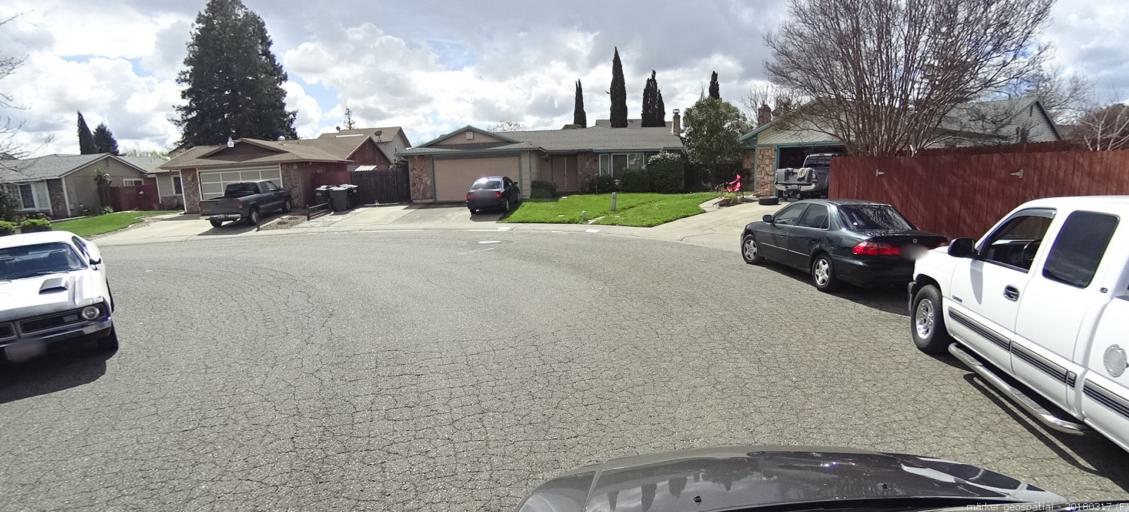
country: US
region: California
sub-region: Sacramento County
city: Florin
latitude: 38.4767
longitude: -121.4071
